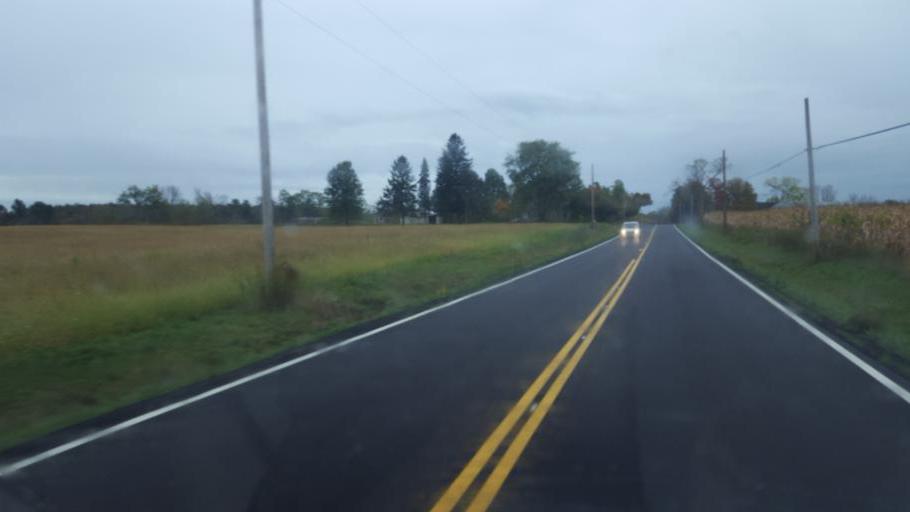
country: US
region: Ohio
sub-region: Huron County
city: New London
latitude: 41.0111
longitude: -82.3847
